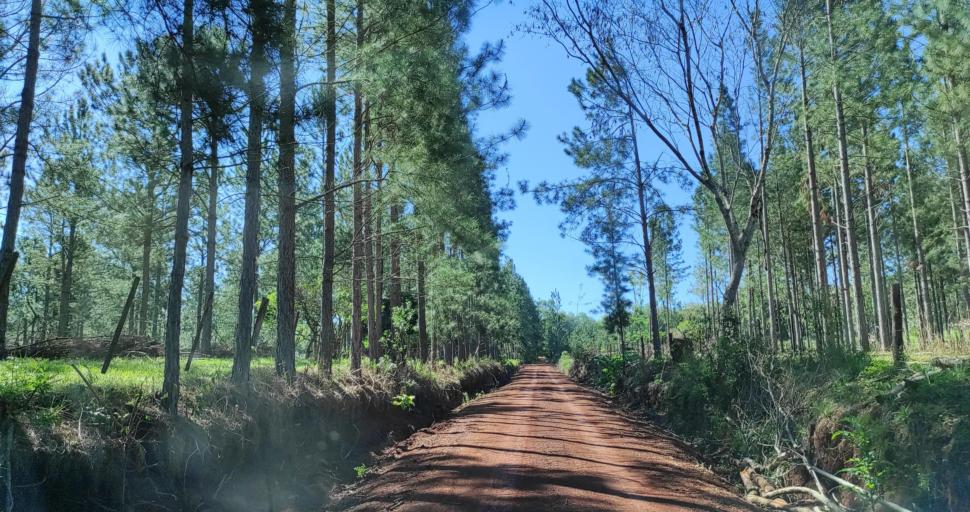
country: AR
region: Misiones
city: Ruiz de Montoya
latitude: -26.9481
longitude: -55.0030
